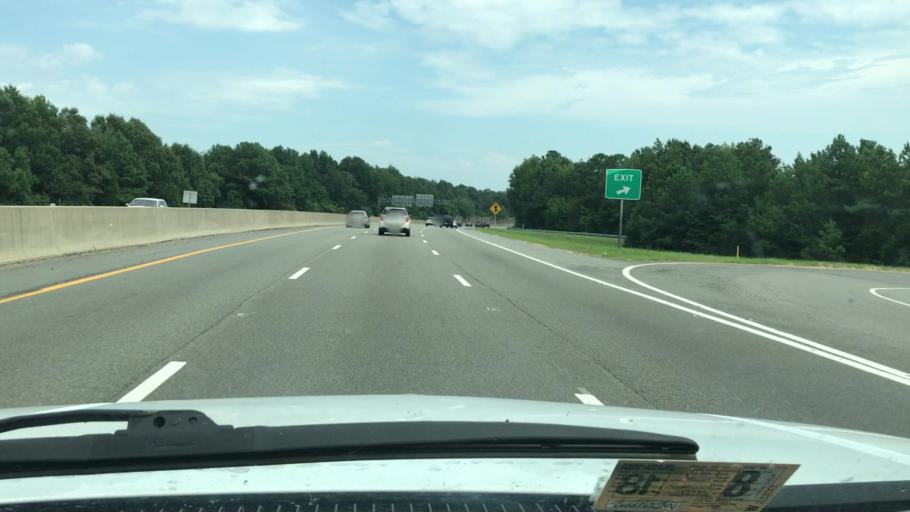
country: US
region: Virginia
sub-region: Chesterfield County
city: Bensley
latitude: 37.4503
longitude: -77.4856
